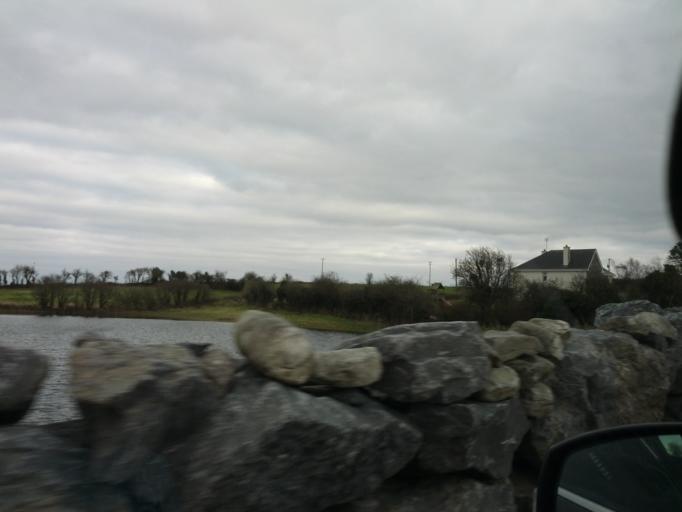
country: IE
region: Connaught
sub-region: County Galway
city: Gort
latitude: 53.1602
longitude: -8.8743
